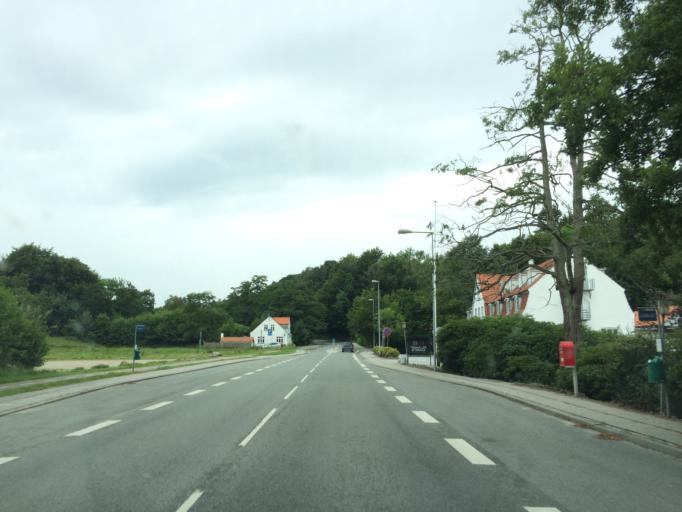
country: DK
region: Central Jutland
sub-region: Syddjurs Kommune
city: Ebeltoft
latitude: 56.2383
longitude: 10.5808
